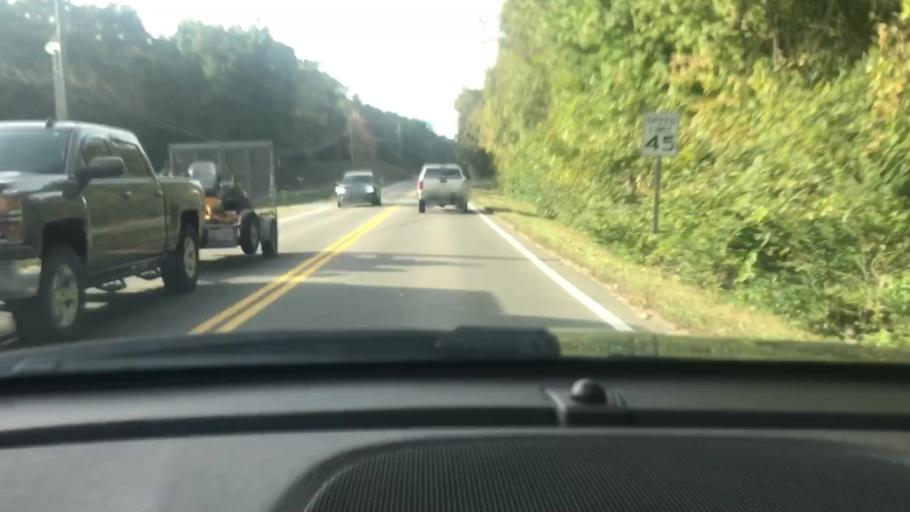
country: US
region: Tennessee
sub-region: Williamson County
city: Fairview
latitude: 35.9922
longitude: -87.1266
